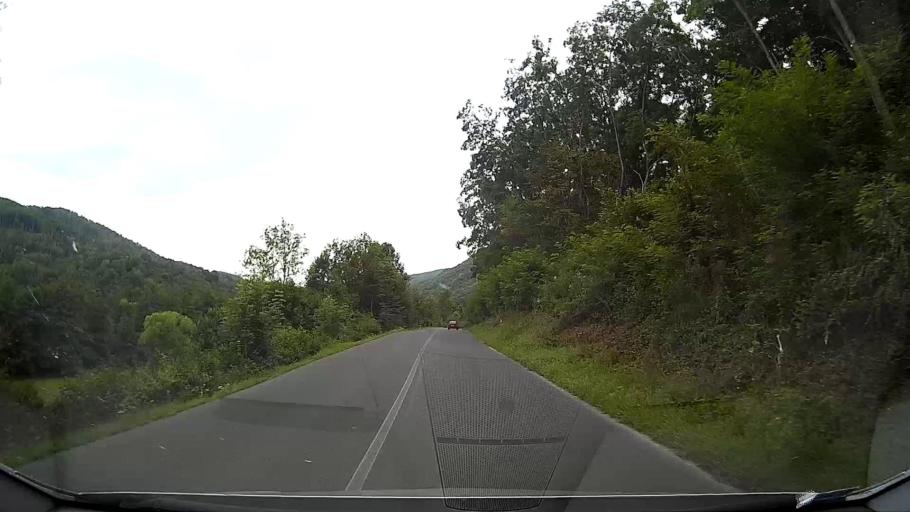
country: SK
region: Banskobystricky
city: Tisovec
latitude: 48.7267
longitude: 20.0200
